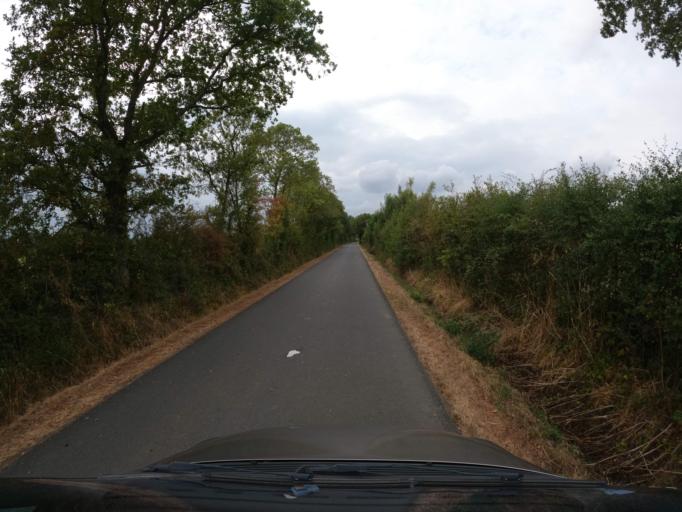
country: FR
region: Pays de la Loire
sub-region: Departement de Maine-et-Loire
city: Saint-Christophe-du-Bois
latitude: 47.0439
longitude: -0.9815
